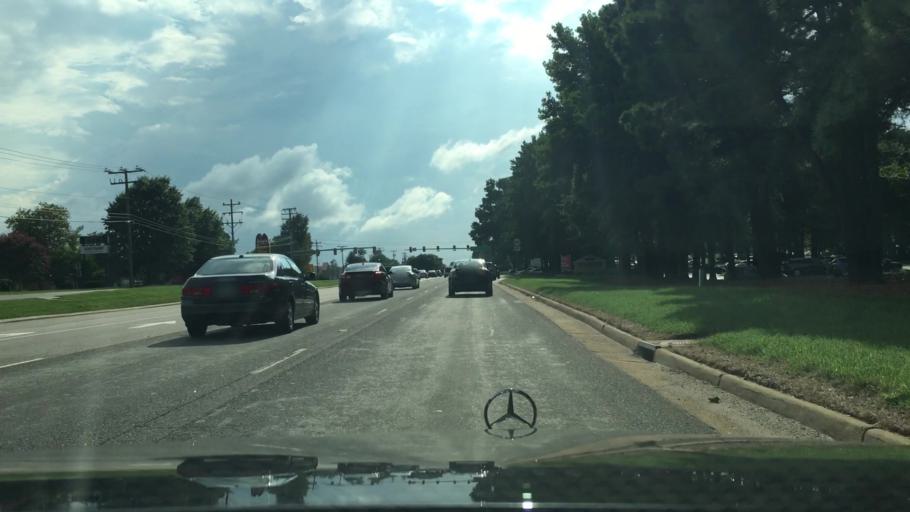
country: US
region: Virginia
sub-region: Chesterfield County
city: Bon Air
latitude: 37.5069
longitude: -77.5961
